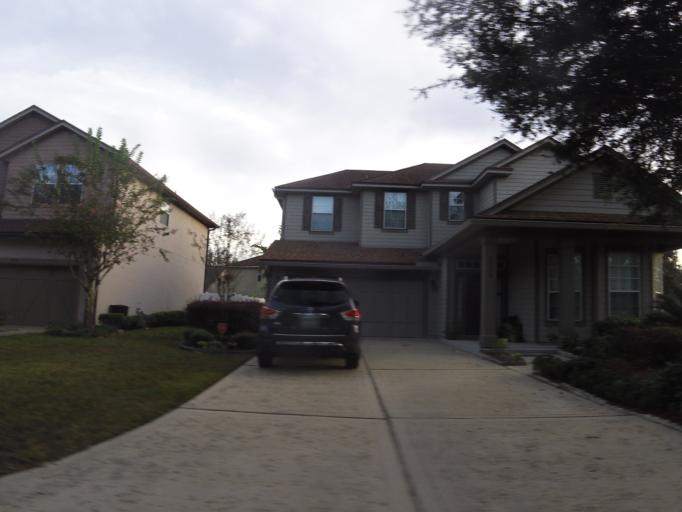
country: US
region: Florida
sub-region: Saint Johns County
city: Fruit Cove
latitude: 30.1509
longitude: -81.5451
